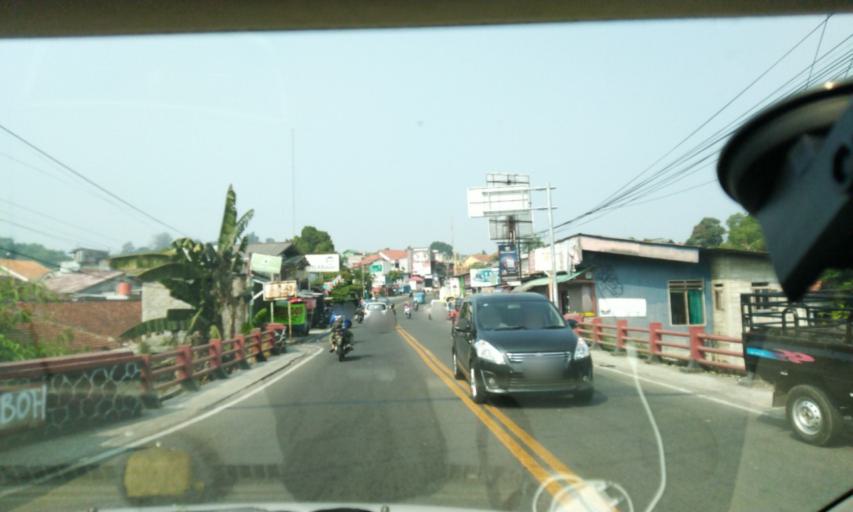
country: ID
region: West Java
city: Caringin
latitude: -6.6614
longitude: 106.8569
